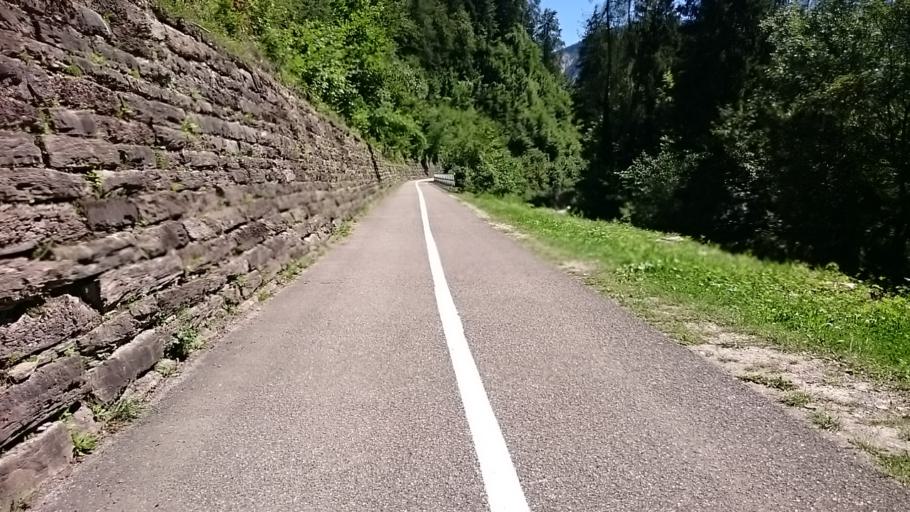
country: IT
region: Veneto
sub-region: Provincia di Belluno
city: Valle di Cadore
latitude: 46.4199
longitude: 12.3116
